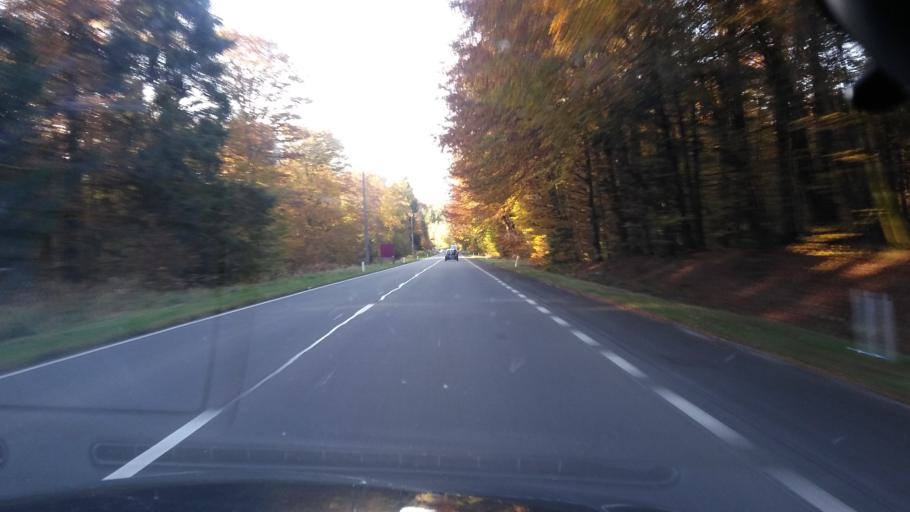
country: BE
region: Wallonia
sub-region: Province du Luxembourg
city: Herbeumont
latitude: 49.7545
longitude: 5.1608
